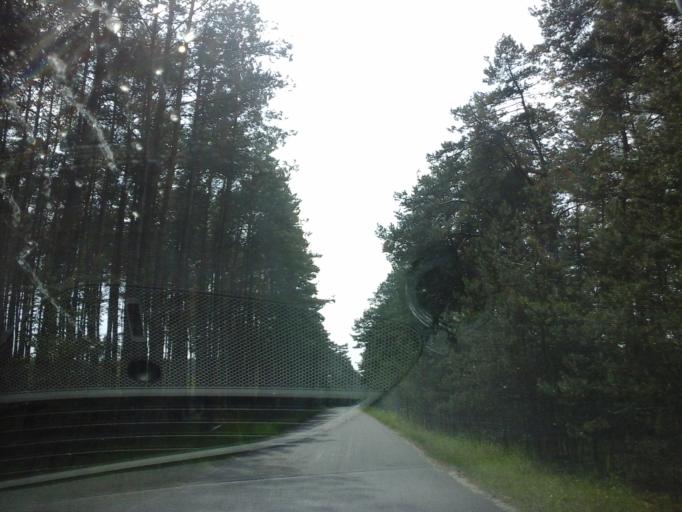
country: PL
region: West Pomeranian Voivodeship
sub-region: Powiat drawski
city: Kalisz Pomorski
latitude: 53.2040
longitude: 15.9364
